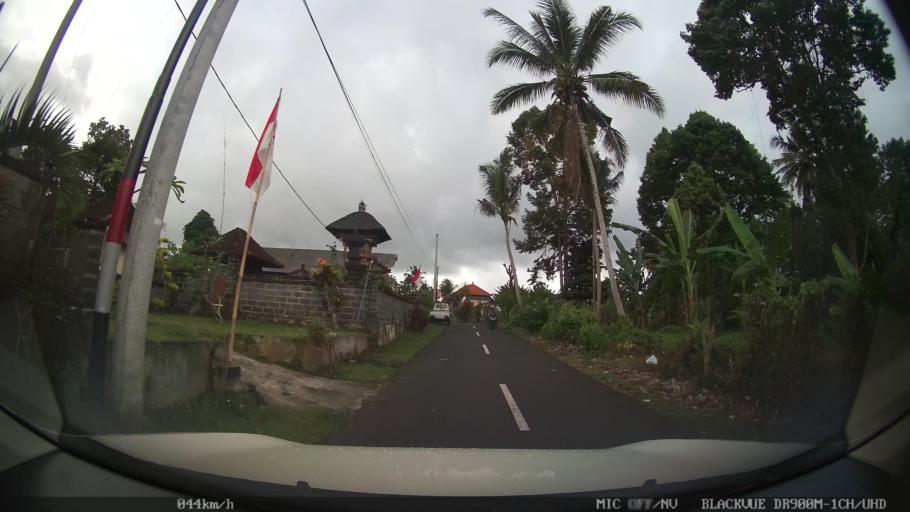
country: ID
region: Bali
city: Banjar Cemenggon
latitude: -8.5350
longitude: 115.1922
